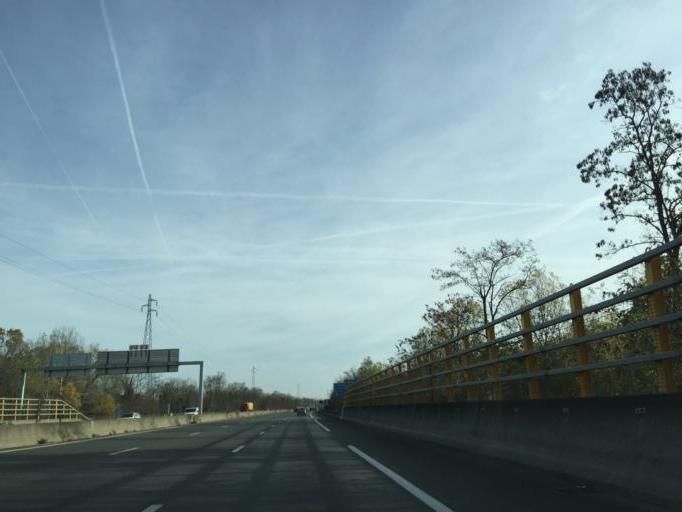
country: FR
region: Rhone-Alpes
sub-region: Departement de l'Ain
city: Miribel
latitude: 45.8120
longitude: 4.9420
